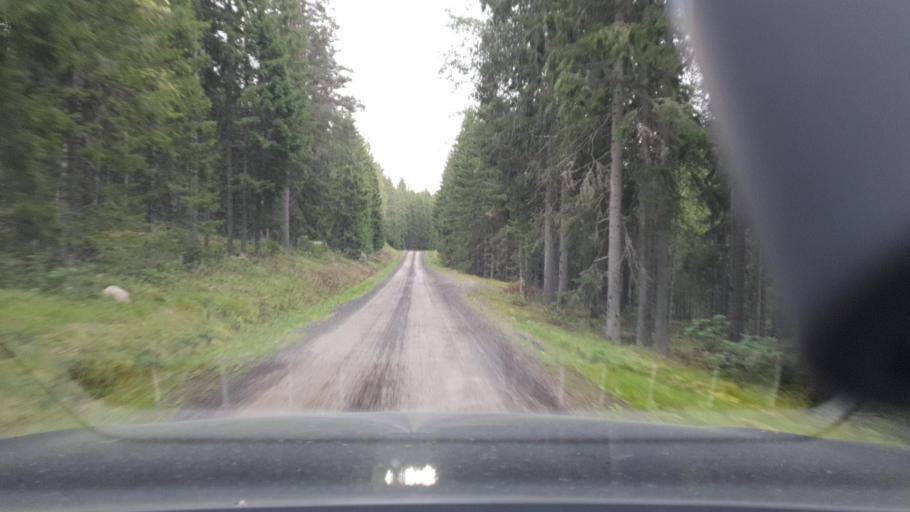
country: SE
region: Vaermland
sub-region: Sunne Kommun
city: Sunne
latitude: 59.8593
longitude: 12.8387
